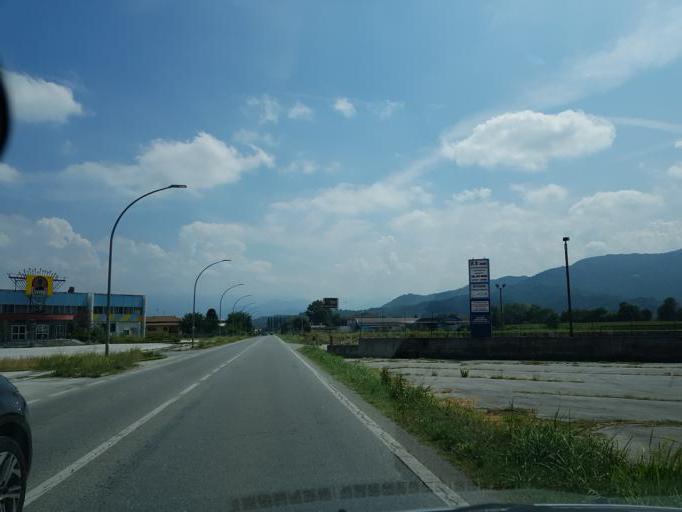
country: IT
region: Piedmont
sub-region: Provincia di Cuneo
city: Caraglio
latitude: 44.4057
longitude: 7.4445
